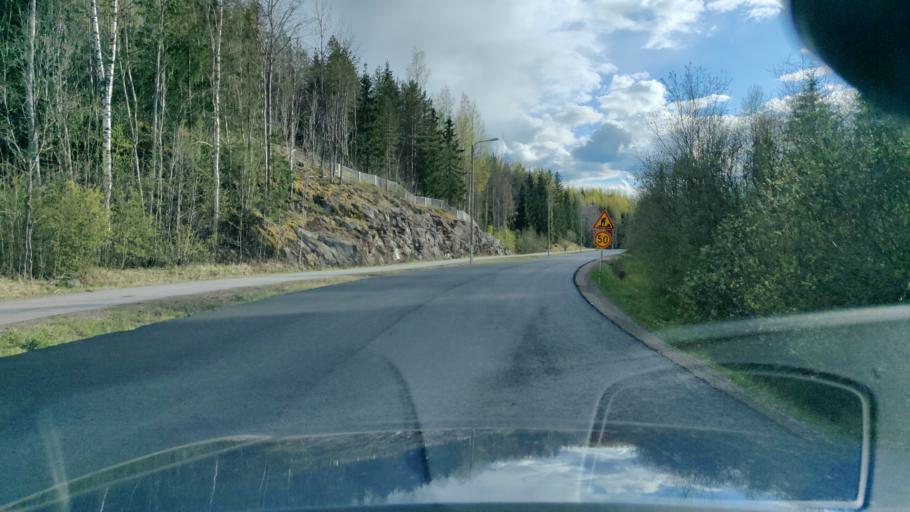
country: FI
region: Uusimaa
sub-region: Helsinki
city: Nurmijaervi
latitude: 60.3755
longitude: 24.7480
